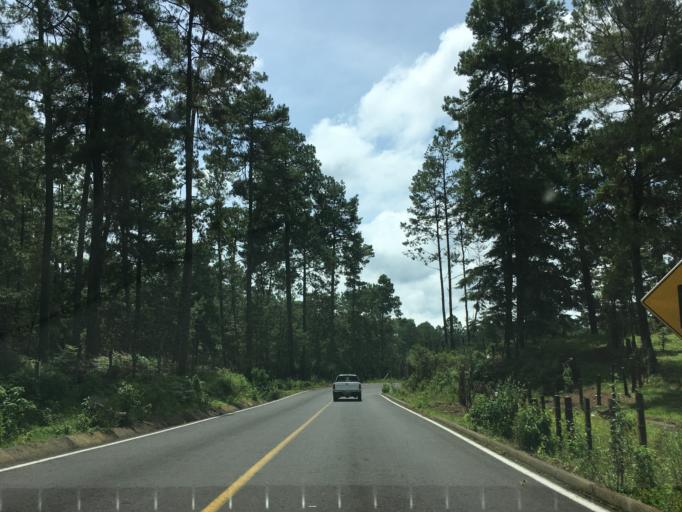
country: MX
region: Michoacan
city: Nuevo San Juan Parangaricutiro
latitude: 19.4457
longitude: -102.1709
